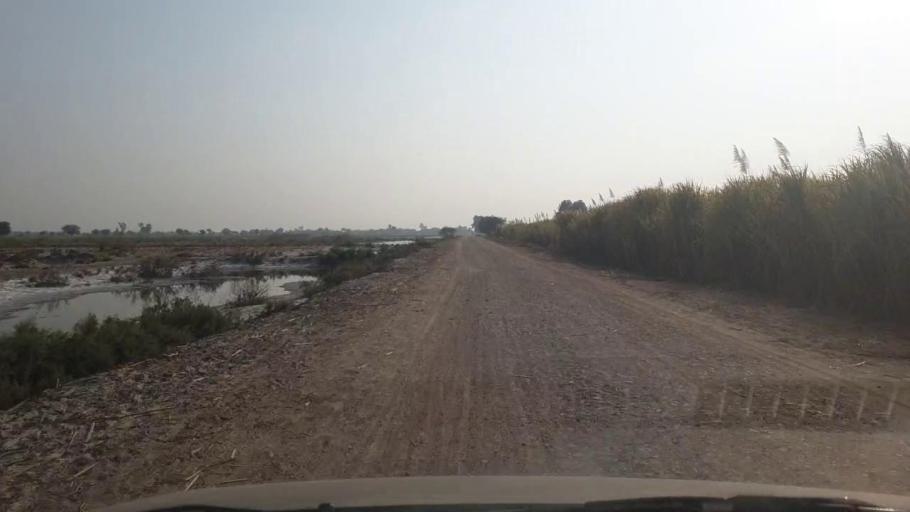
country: PK
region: Sindh
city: Digri
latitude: 25.2600
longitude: 69.1634
